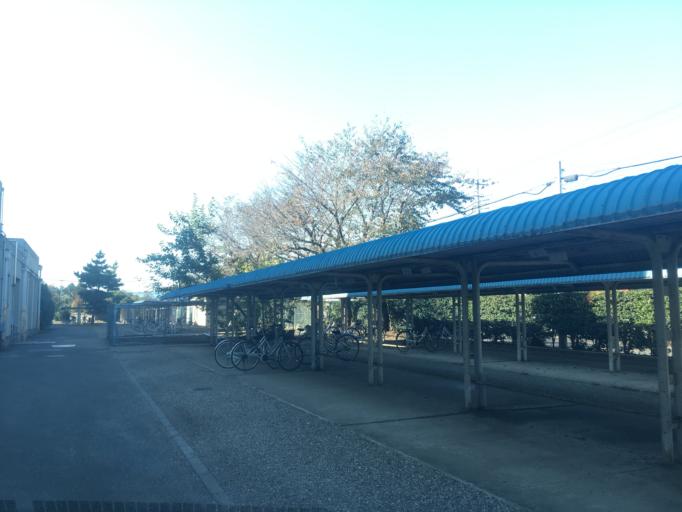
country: JP
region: Saitama
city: Sakado
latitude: 35.9671
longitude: 139.4292
